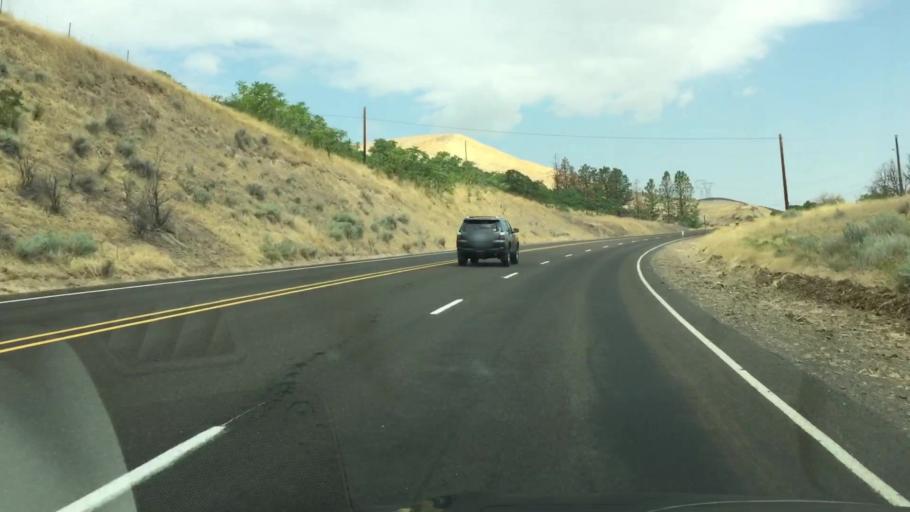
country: US
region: Oregon
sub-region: Wasco County
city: The Dalles
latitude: 45.5695
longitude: -121.1049
